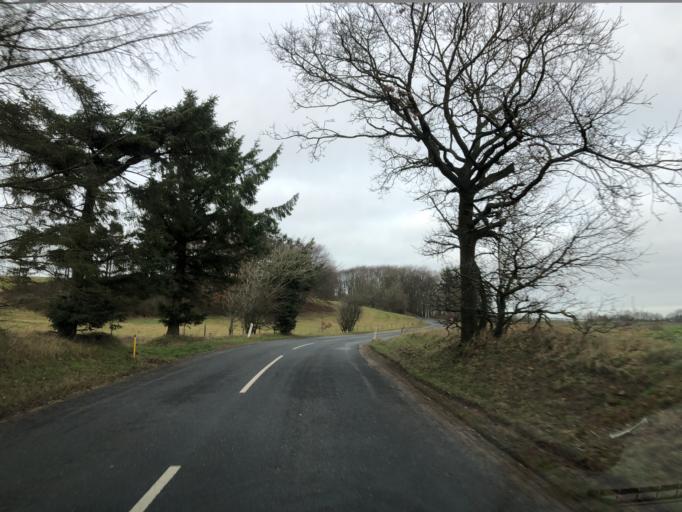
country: DK
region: Central Jutland
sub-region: Viborg Kommune
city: Stoholm
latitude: 56.4372
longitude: 9.1058
